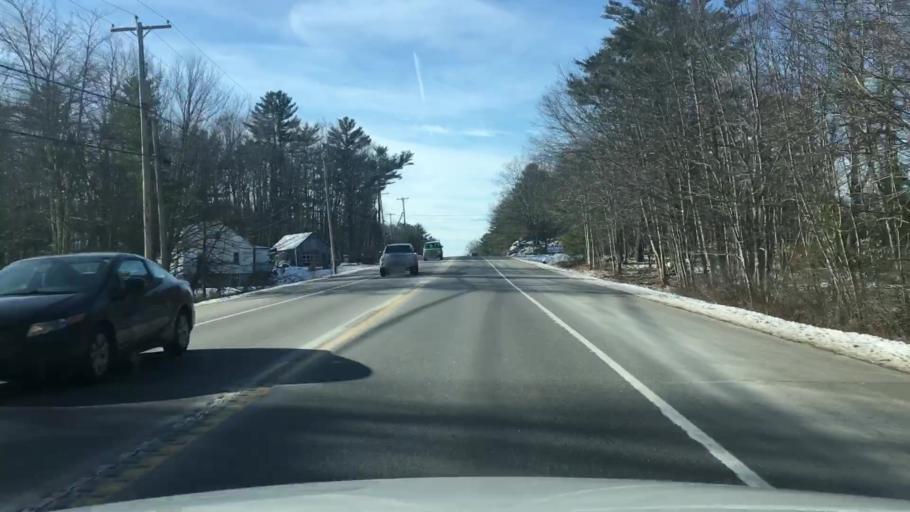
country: US
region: Maine
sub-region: Sagadahoc County
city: Woolwich
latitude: 43.9563
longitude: -69.7354
